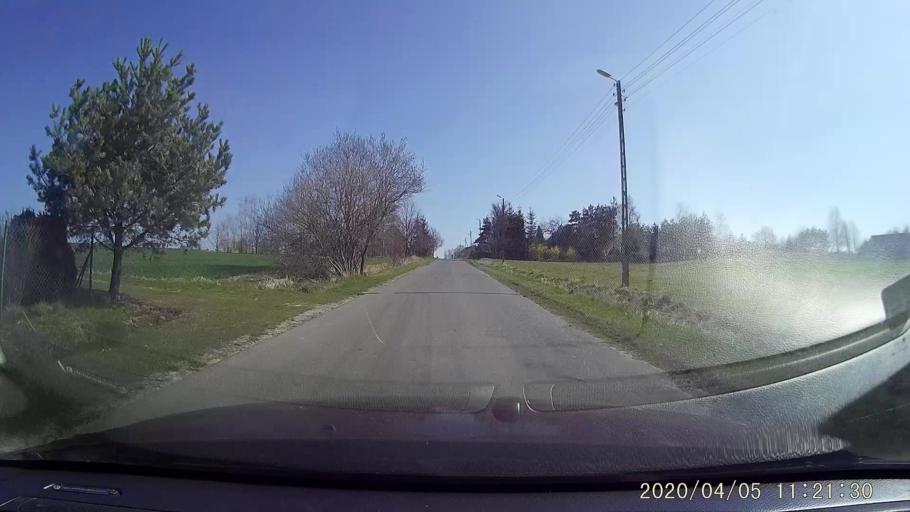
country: PL
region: Lower Silesian Voivodeship
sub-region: Powiat zgorzelecki
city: Sulikow
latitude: 51.0539
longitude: 15.1213
